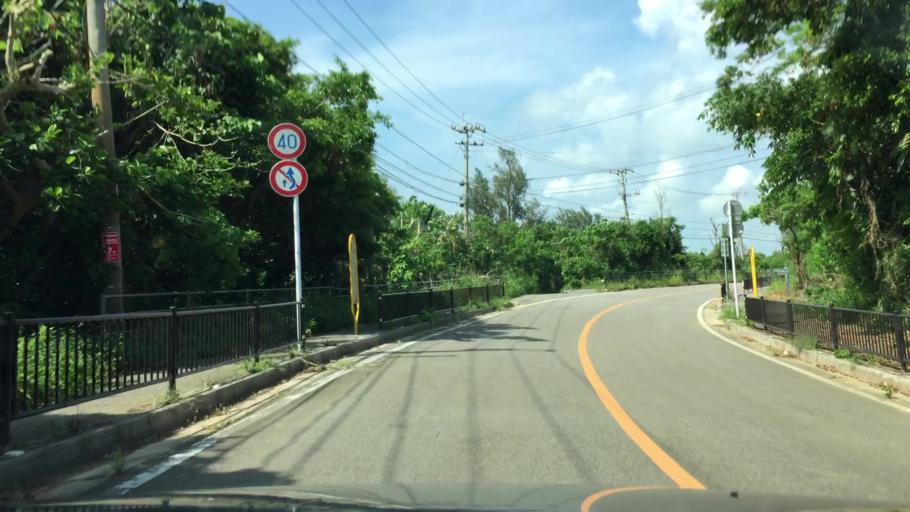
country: JP
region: Okinawa
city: Ishigaki
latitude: 24.4964
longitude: 124.2339
